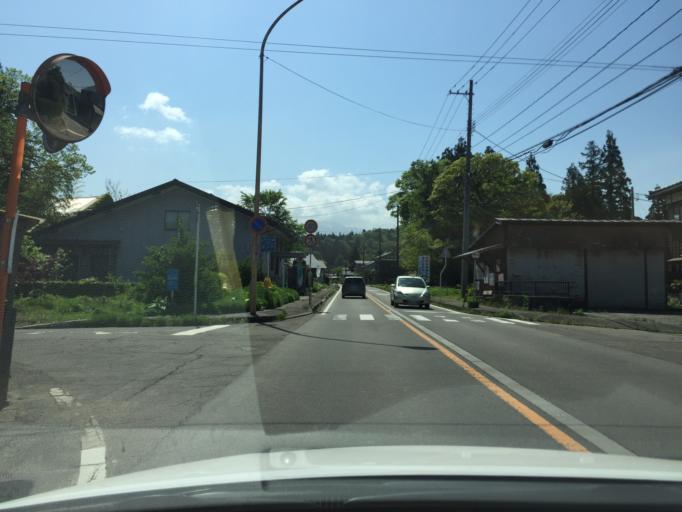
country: JP
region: Niigata
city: Kamo
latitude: 37.6294
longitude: 139.0963
